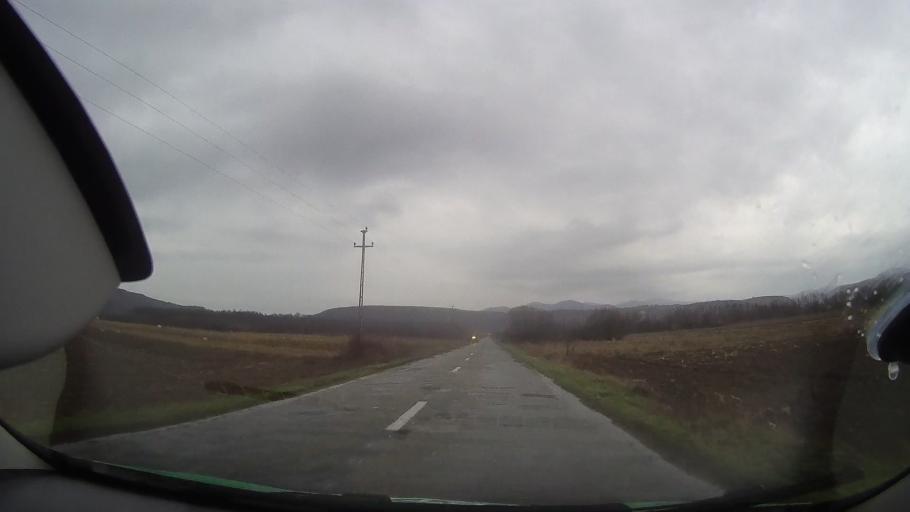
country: RO
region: Bihor
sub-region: Comuna Soimi
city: Soimi
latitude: 46.6891
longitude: 22.1039
